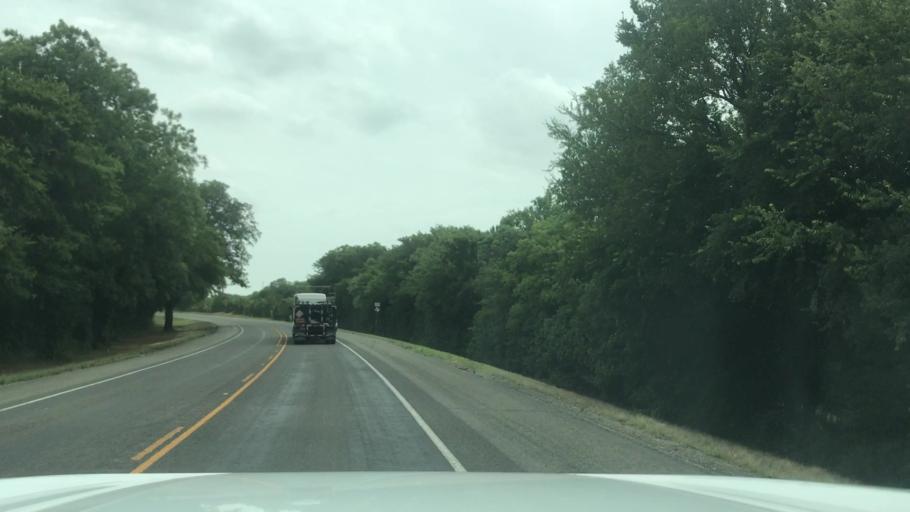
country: US
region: Texas
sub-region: Bosque County
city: Valley Mills
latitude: 31.6784
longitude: -97.5239
